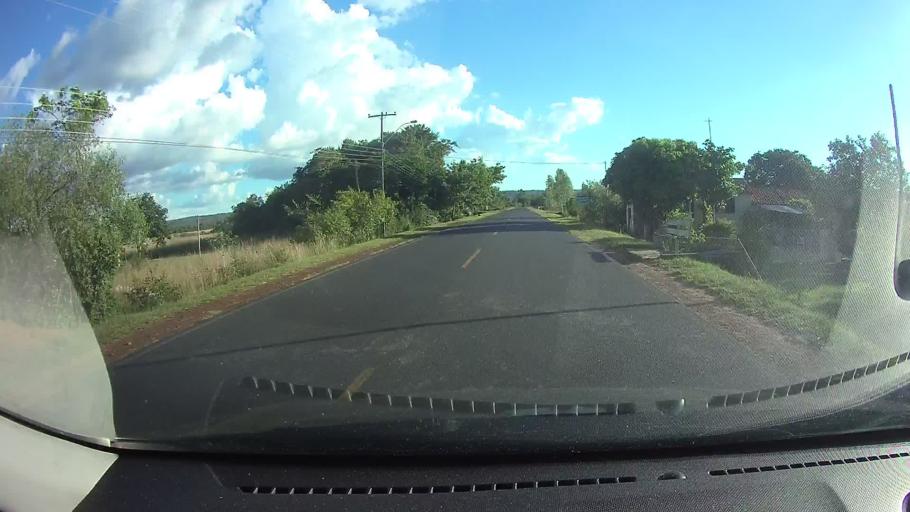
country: PY
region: Cordillera
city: Emboscada
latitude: -25.1537
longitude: -57.2614
